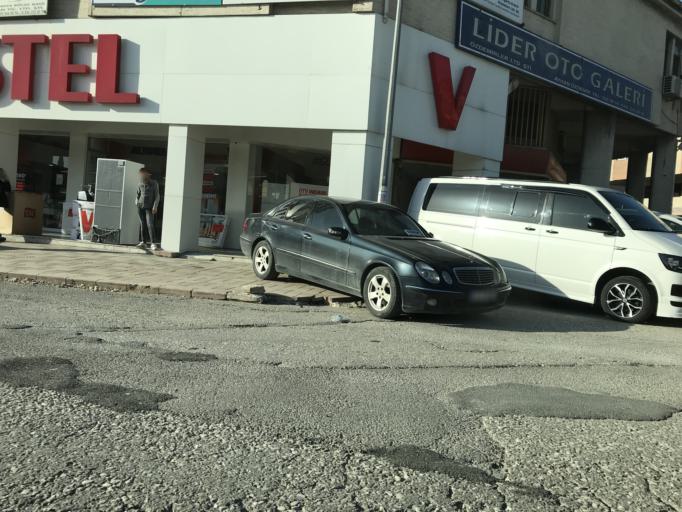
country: TR
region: Hatay
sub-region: Antakya Ilcesi
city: Antakya
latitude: 36.2081
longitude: 36.1682
